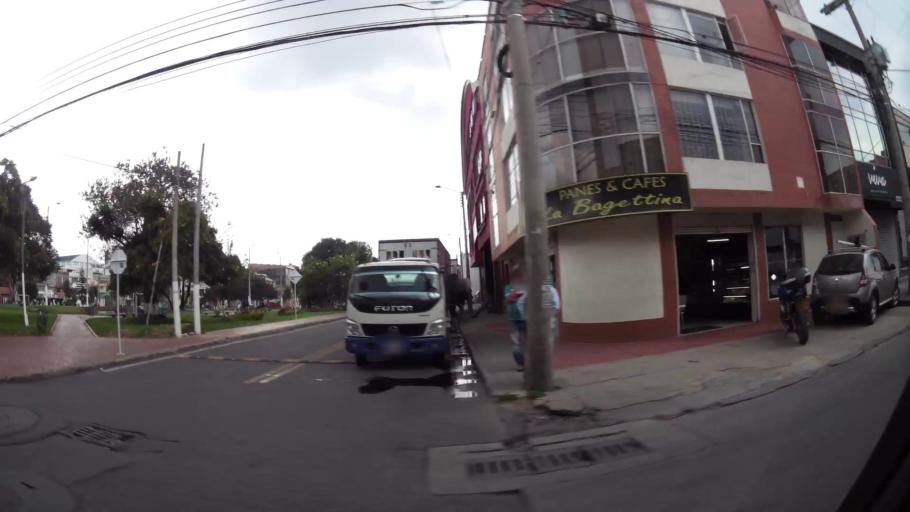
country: CO
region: Cundinamarca
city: La Calera
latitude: 4.7494
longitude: -74.0432
